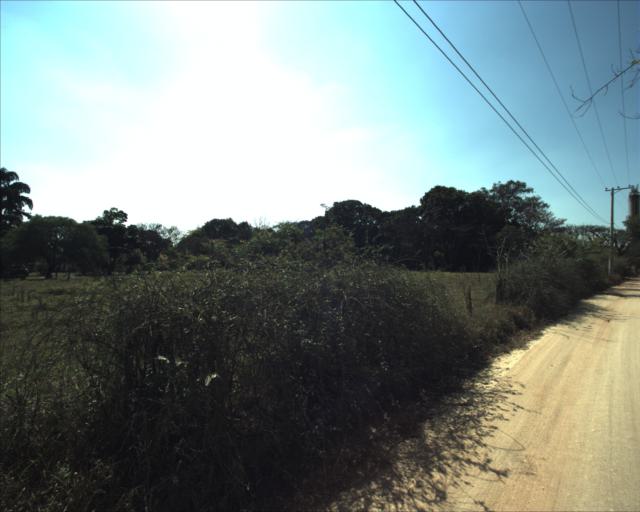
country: BR
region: Sao Paulo
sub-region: Aracoiaba Da Serra
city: Aracoiaba da Serra
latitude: -23.4874
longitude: -47.5448
